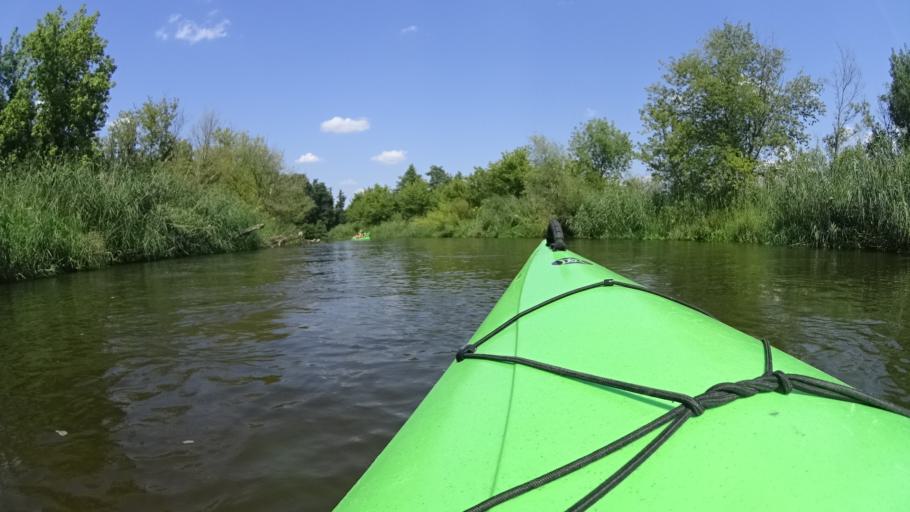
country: PL
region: Masovian Voivodeship
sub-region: Powiat bialobrzeski
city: Wysmierzyce
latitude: 51.6593
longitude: 20.8580
